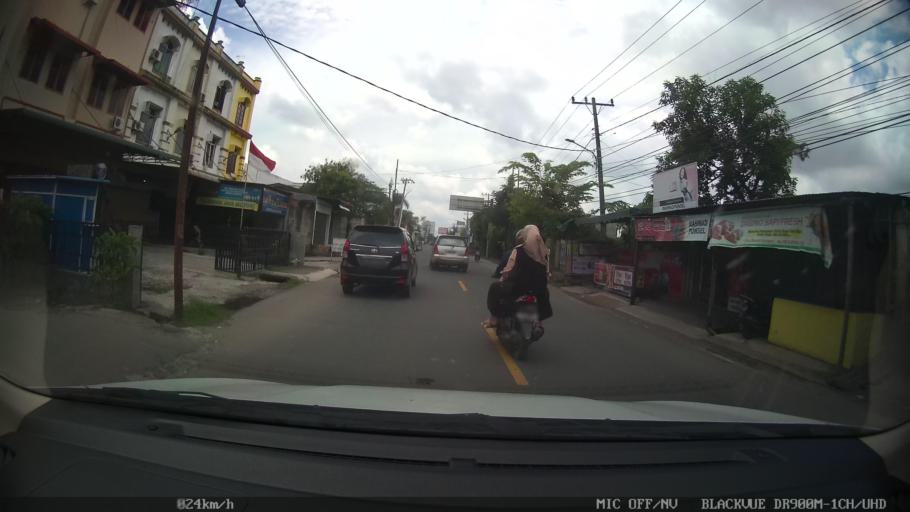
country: ID
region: North Sumatra
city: Medan
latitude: 3.6271
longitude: 98.7078
